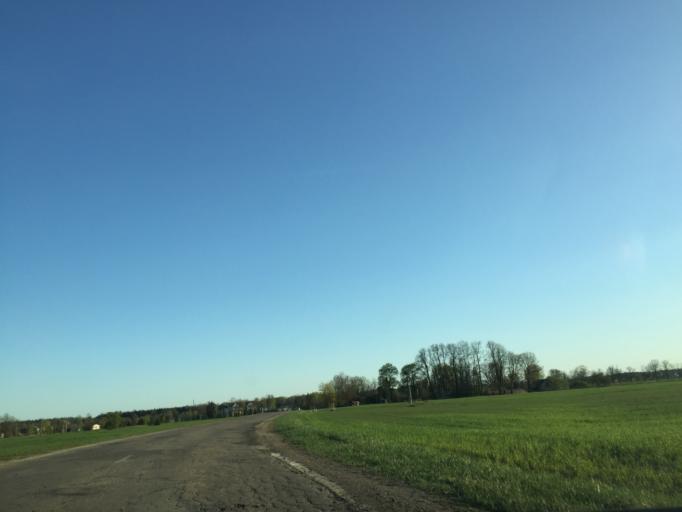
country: LV
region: Koknese
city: Koknese
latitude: 56.6836
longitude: 25.4868
